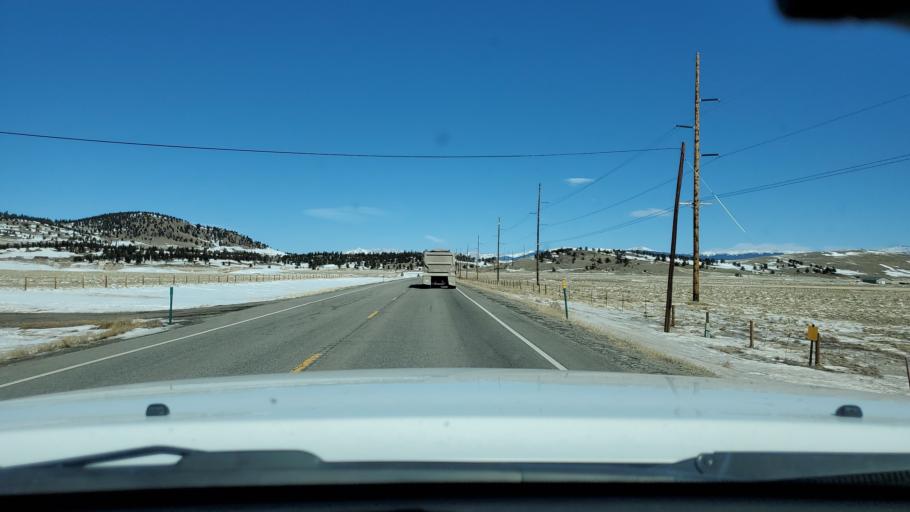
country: US
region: Colorado
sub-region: Park County
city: Fairplay
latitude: 39.2902
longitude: -105.9076
